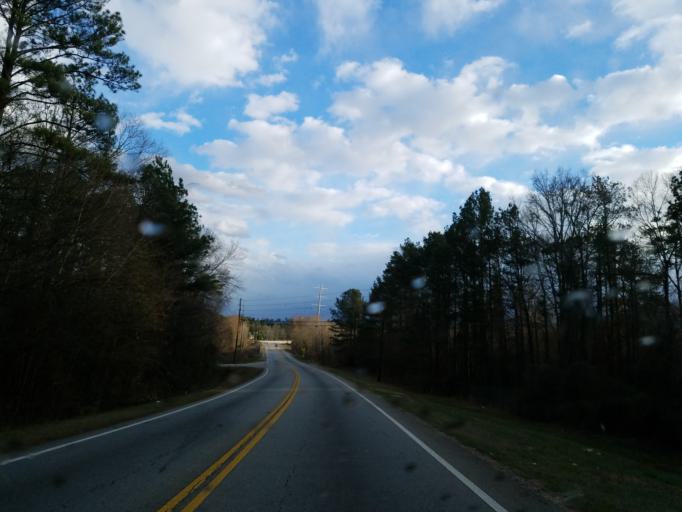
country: US
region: Georgia
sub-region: Henry County
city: Stockbridge
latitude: 33.5255
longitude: -84.1961
